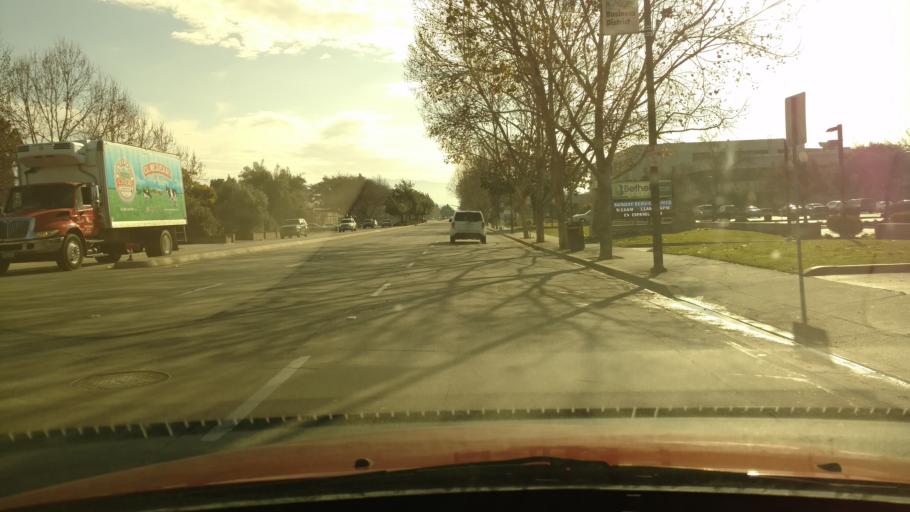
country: US
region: California
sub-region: Santa Clara County
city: Campbell
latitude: 37.3043
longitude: -121.9501
